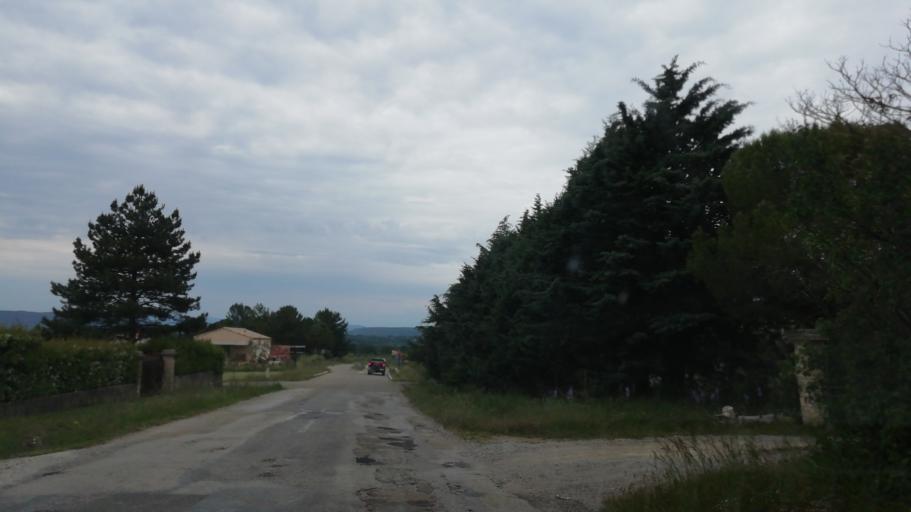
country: FR
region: Languedoc-Roussillon
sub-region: Departement de l'Herault
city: Saint-Martin-de-Londres
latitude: 43.7865
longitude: 3.7580
